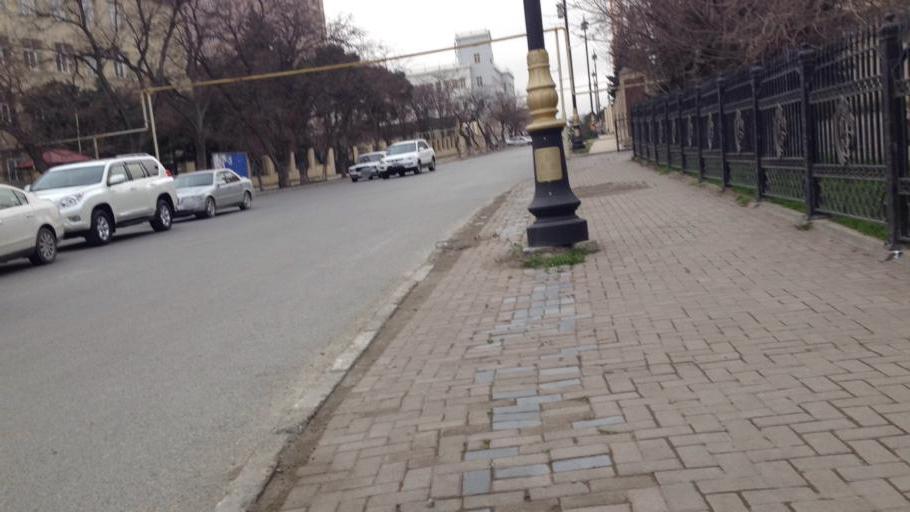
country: AZ
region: Baki
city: Baku
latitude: 40.3893
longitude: 49.8501
